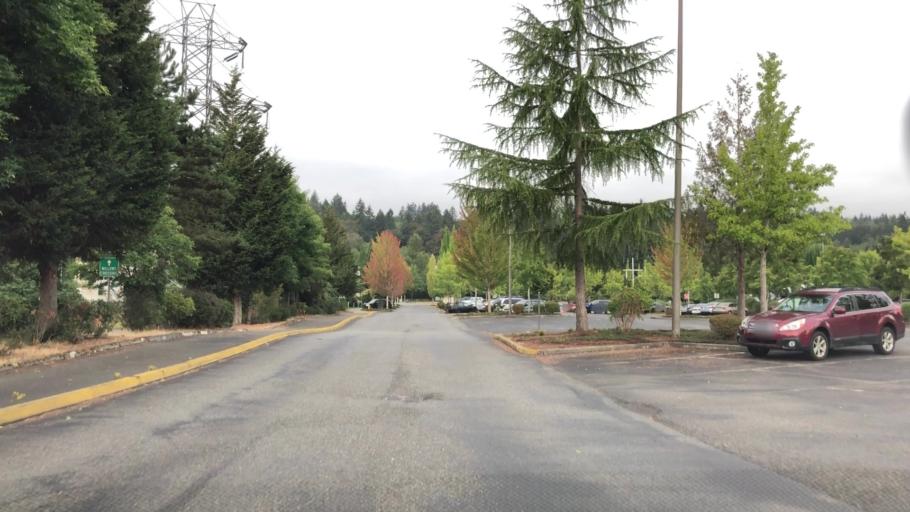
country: US
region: Washington
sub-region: King County
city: Redmond
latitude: 47.6886
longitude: -122.1449
